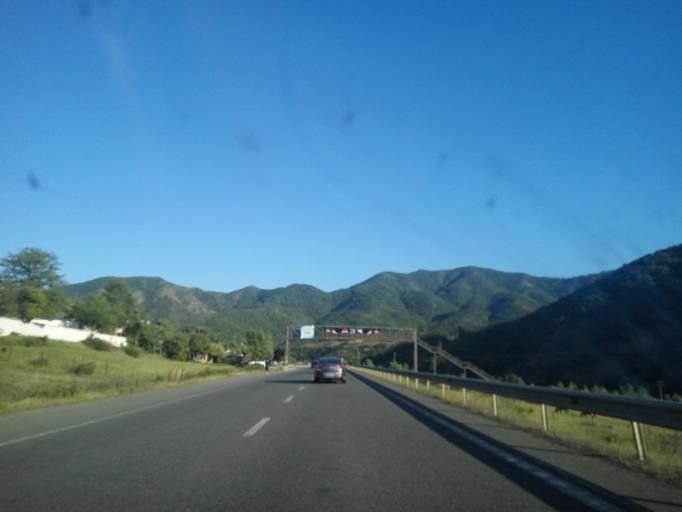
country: AL
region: Lezhe
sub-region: Rrethi i Mirdites
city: Rubik
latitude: 41.7879
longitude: 19.8185
